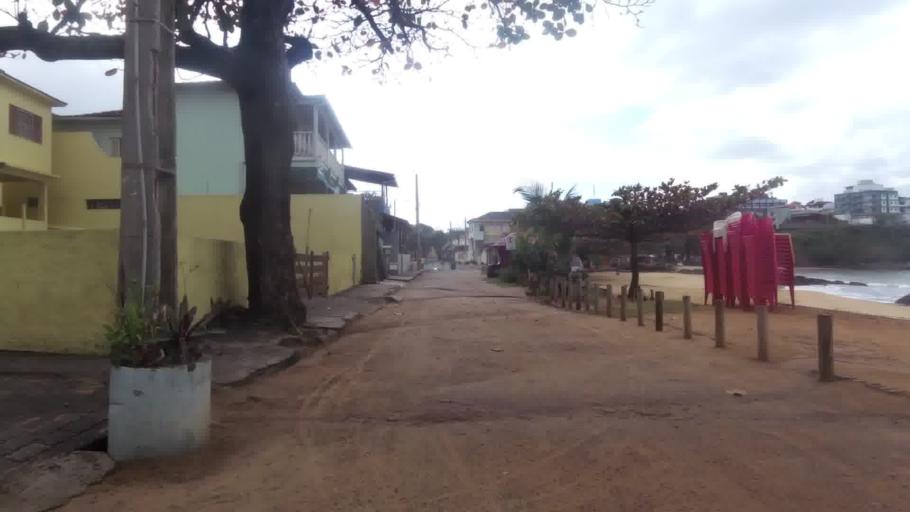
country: BR
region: Espirito Santo
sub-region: Piuma
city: Piuma
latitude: -20.8331
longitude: -40.6980
